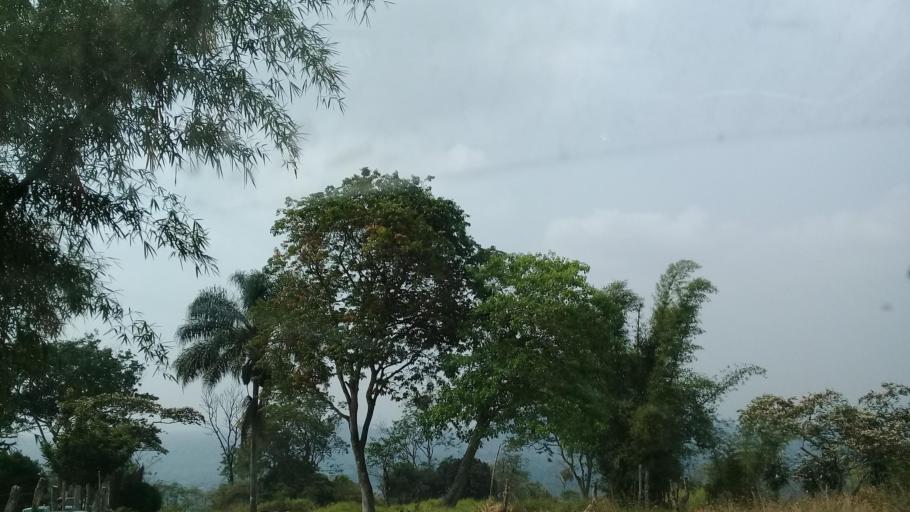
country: MX
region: Veracruz
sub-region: Xalapa
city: Fraccionamiento las Fuentes
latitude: 19.4901
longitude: -96.8983
